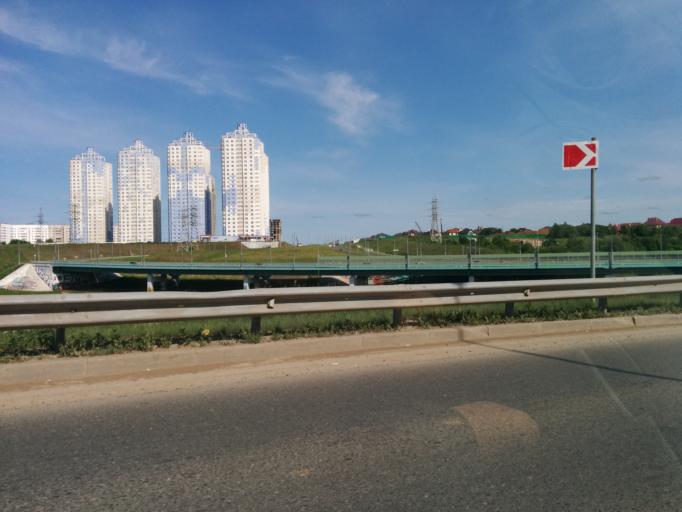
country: RU
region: Perm
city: Perm
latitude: 58.0045
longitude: 56.3131
